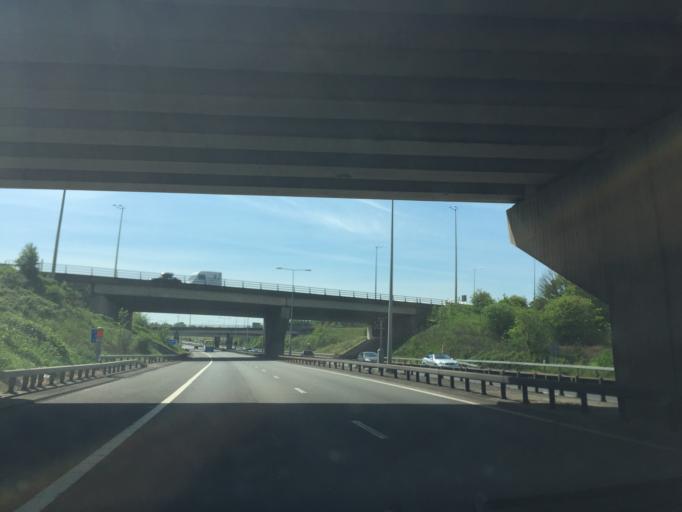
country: GB
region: England
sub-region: Essex
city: Epping
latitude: 51.6802
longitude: 0.1262
